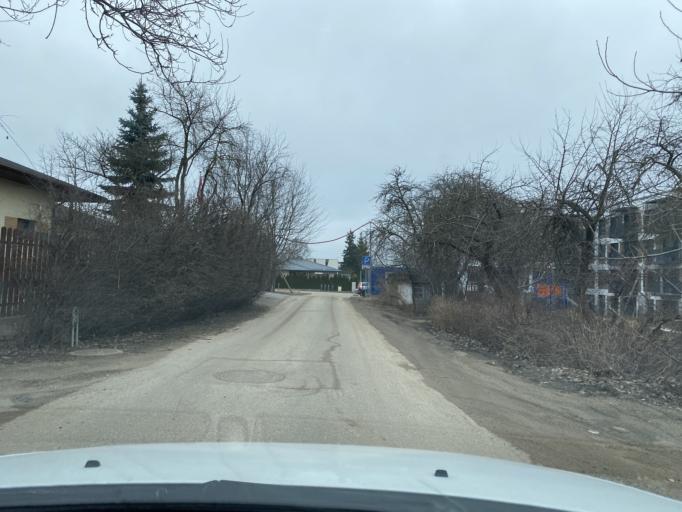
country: LT
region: Vilnius County
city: Seskine
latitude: 54.7181
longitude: 25.2690
